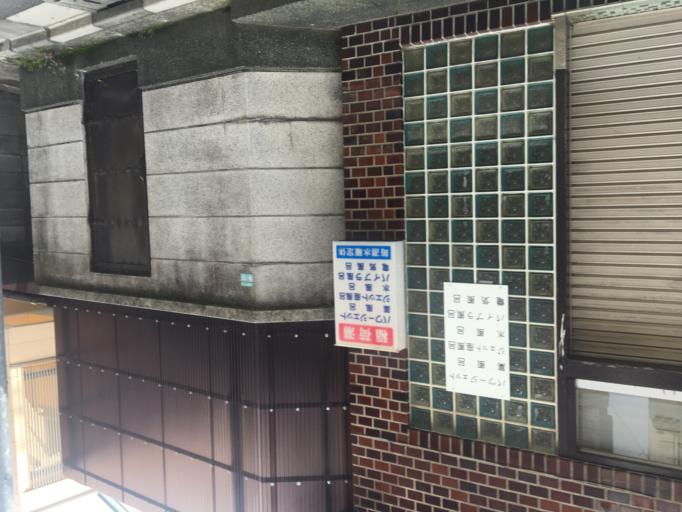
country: JP
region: Tokyo
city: Tokyo
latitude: 35.7346
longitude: 139.7192
